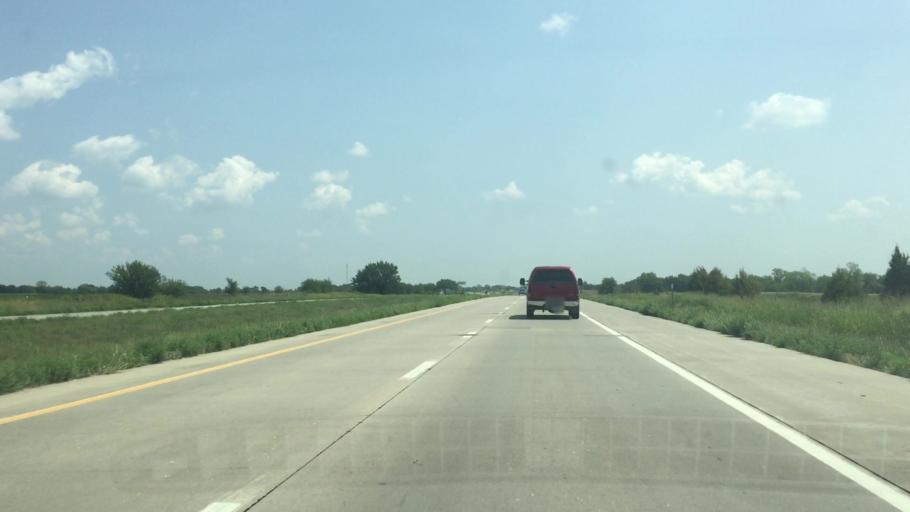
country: US
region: Kansas
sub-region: Franklin County
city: Wellsville
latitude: 38.6772
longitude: -95.1371
